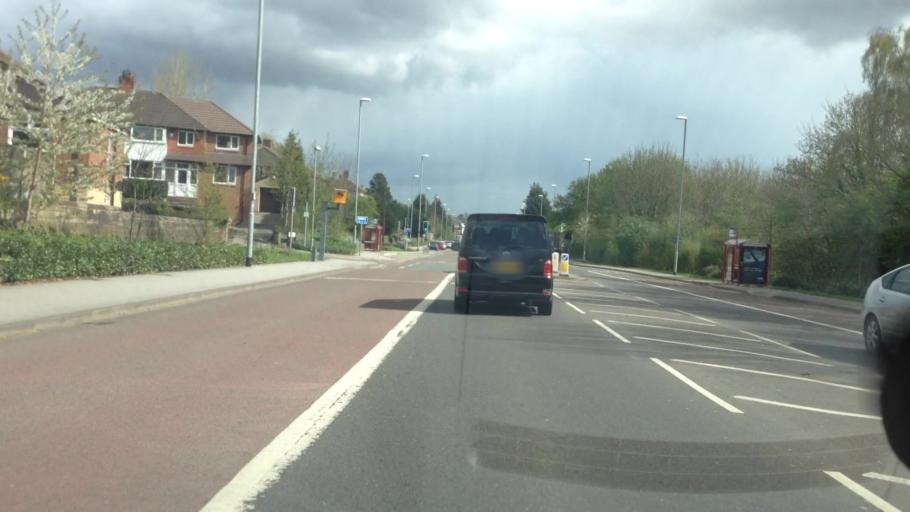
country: GB
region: England
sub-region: City and Borough of Leeds
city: Leeds
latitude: 53.8111
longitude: -1.5959
